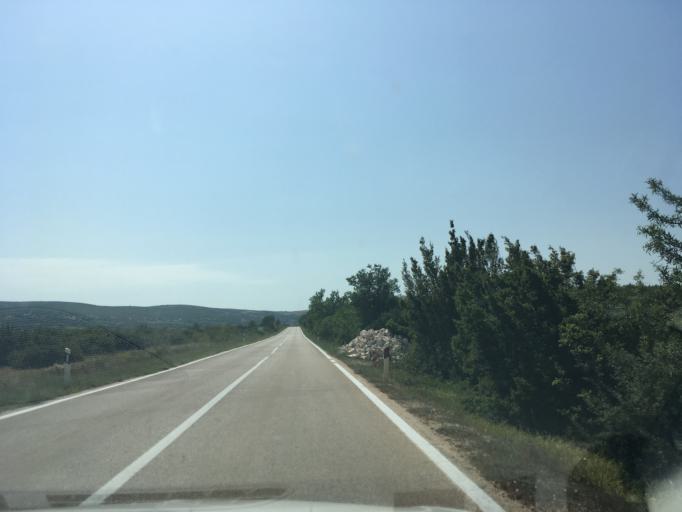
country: HR
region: Zadarska
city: Benkovac
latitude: 43.9654
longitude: 15.7385
